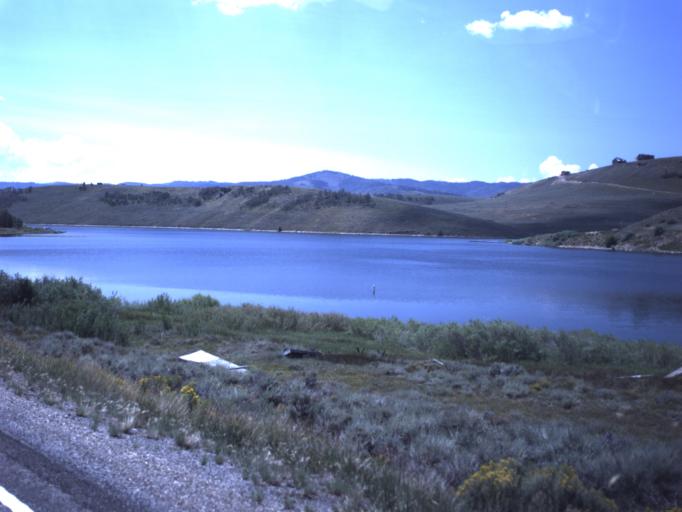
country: US
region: Utah
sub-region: Carbon County
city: Helper
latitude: 39.8104
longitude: -111.1351
